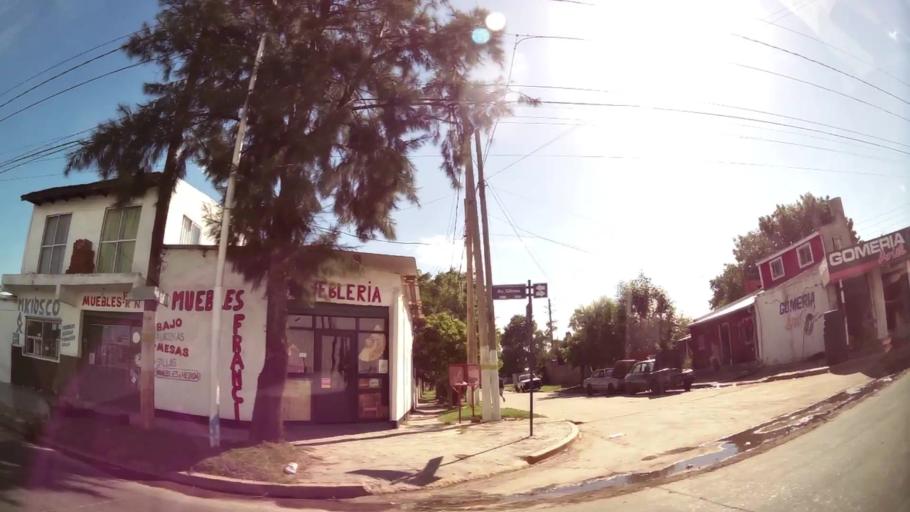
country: AR
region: Buenos Aires
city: Santa Catalina - Dique Lujan
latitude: -34.4662
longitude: -58.7122
